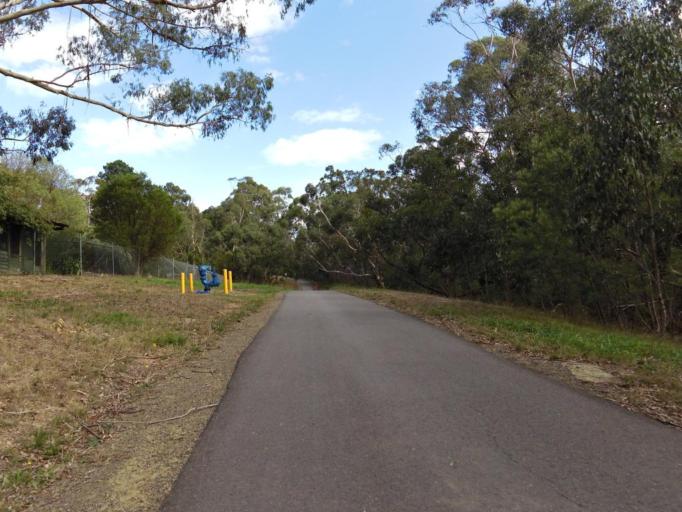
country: AU
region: Victoria
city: Mitcham
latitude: -37.7981
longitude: 145.2039
